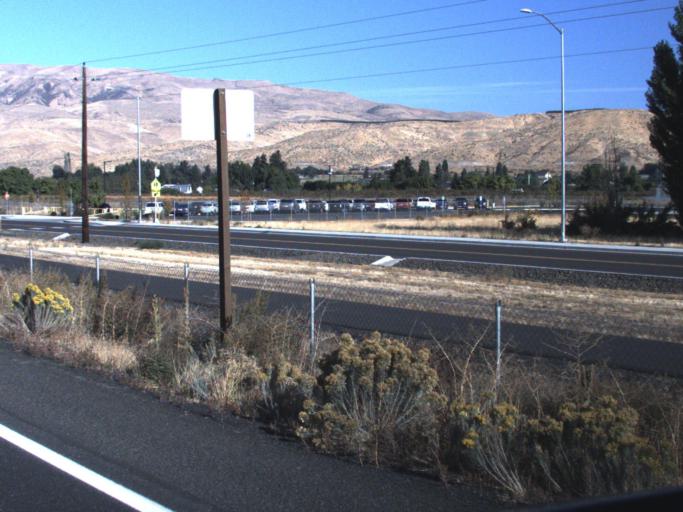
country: US
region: Washington
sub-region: Yakima County
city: Tieton
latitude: 46.7222
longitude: -120.6858
